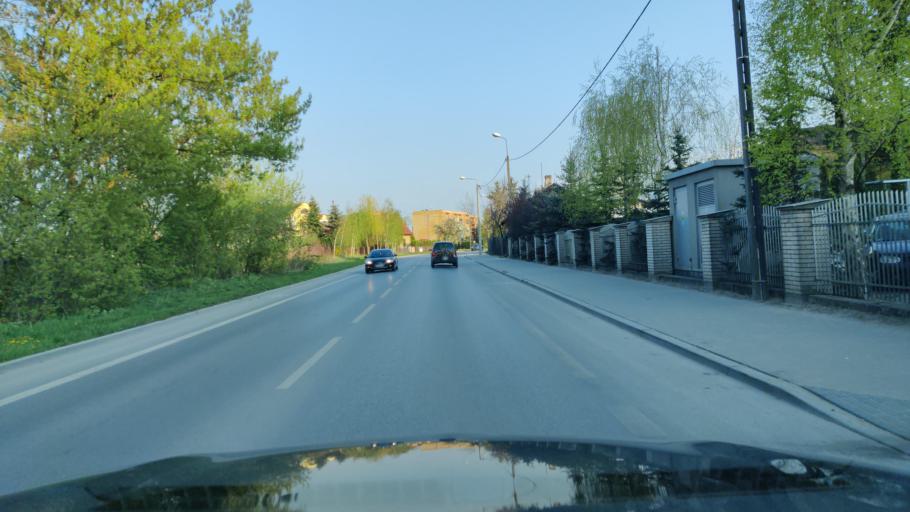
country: PL
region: Masovian Voivodeship
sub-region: Powiat pultuski
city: Pultusk
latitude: 52.6989
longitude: 21.0789
